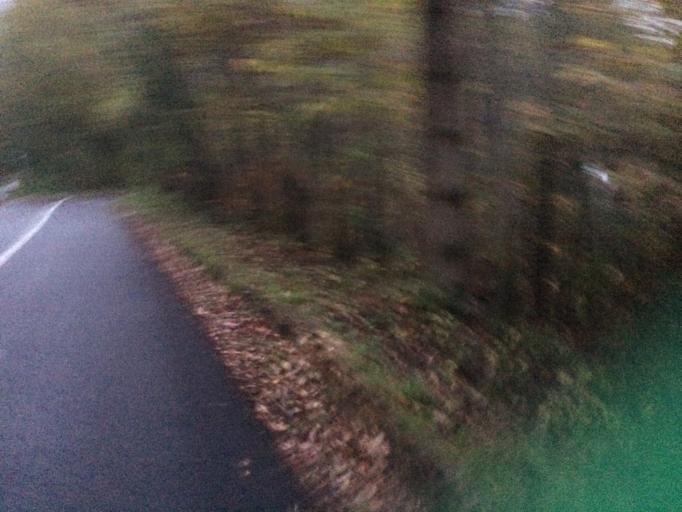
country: FR
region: Ile-de-France
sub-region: Departement de l'Essonne
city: La Ville-du-Bois
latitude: 48.6567
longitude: 2.2574
